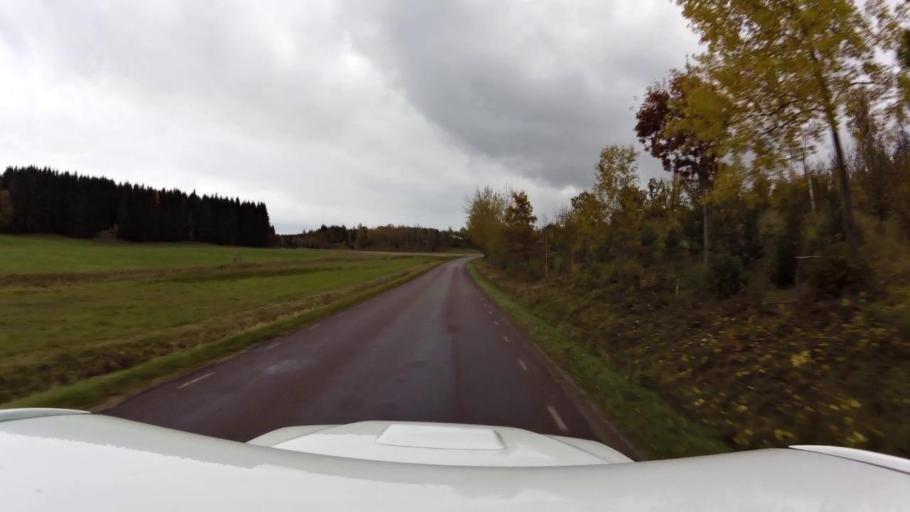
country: SE
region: OEstergoetland
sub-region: Linkopings Kommun
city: Ljungsbro
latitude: 58.5462
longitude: 15.5248
